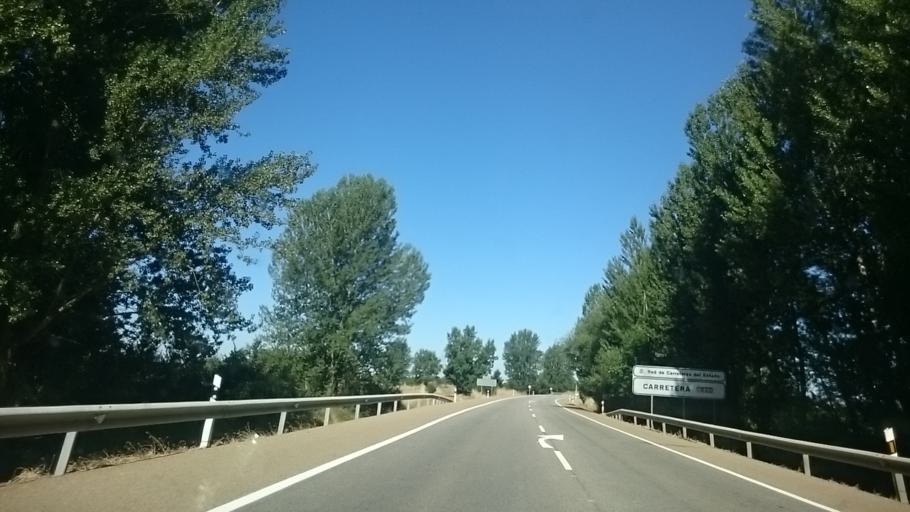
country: ES
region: Castille and Leon
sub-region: Provincia de Leon
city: Mansilla de las Mulas
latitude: 42.5031
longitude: -5.4165
